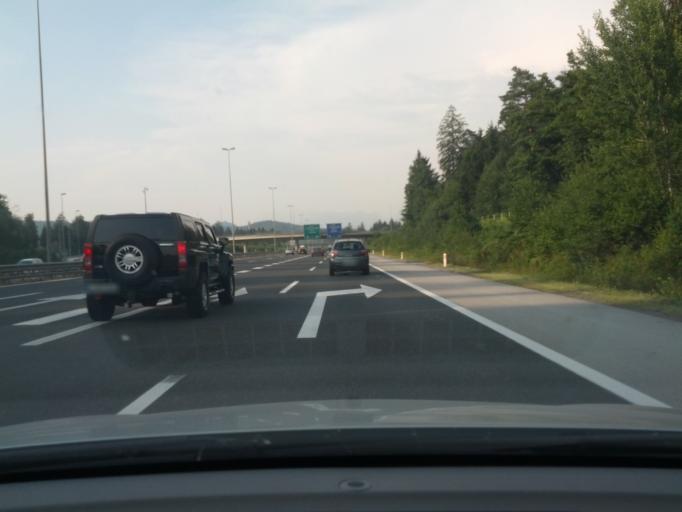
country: SI
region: Ljubljana
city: Ljubljana
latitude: 46.0647
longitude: 14.4566
